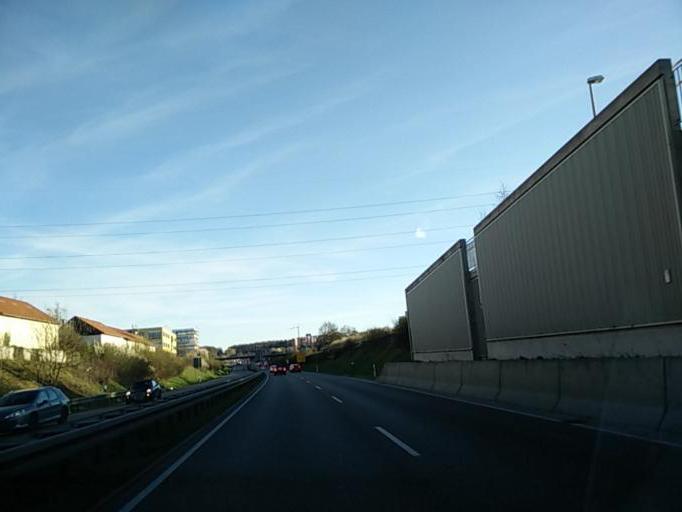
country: DE
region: Baden-Wuerttemberg
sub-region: Regierungsbezirk Stuttgart
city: Holzgerlingen
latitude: 48.6441
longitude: 9.0081
